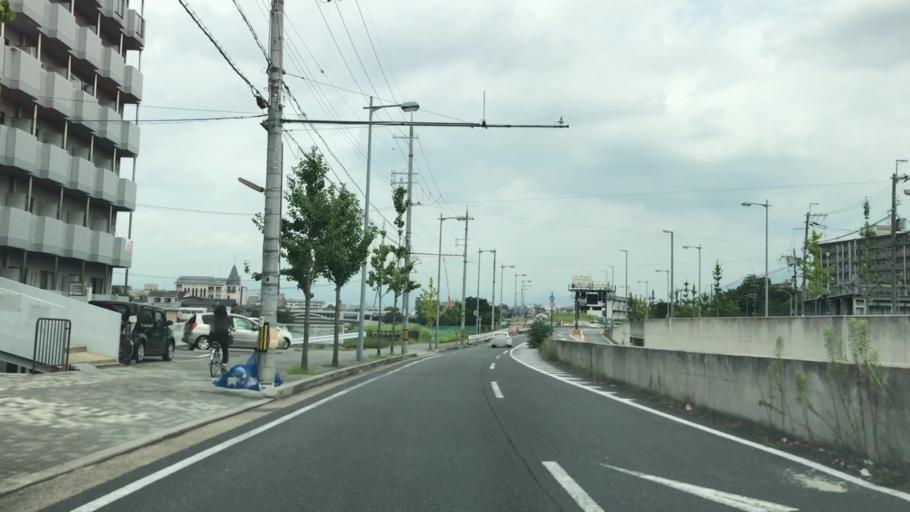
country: JP
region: Kyoto
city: Kyoto
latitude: 34.9752
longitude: 135.7676
